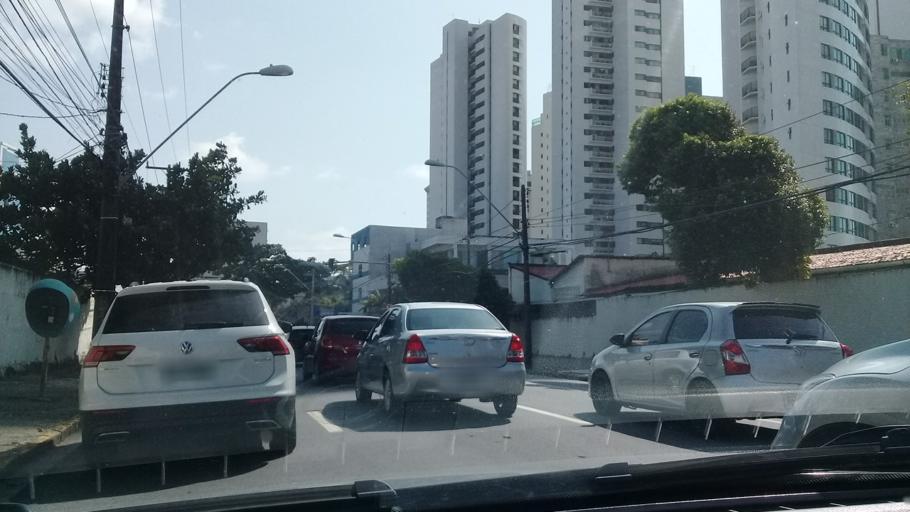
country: BR
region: Pernambuco
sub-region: Recife
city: Recife
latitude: -8.0933
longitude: -34.8840
